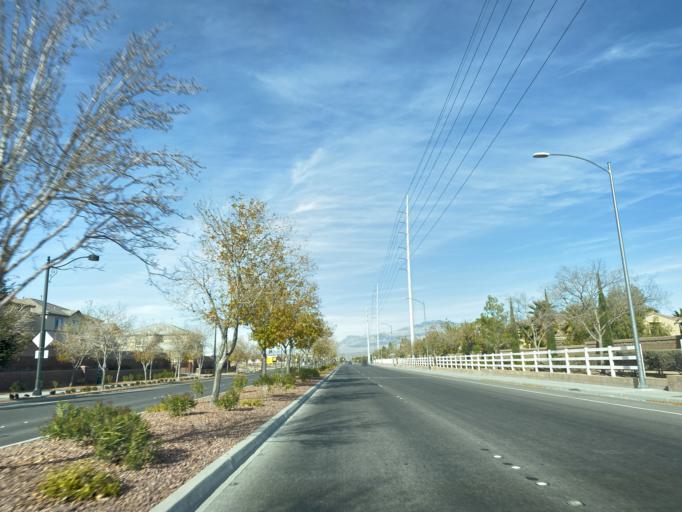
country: US
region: Nevada
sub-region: Clark County
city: Summerlin South
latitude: 36.3040
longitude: -115.3149
